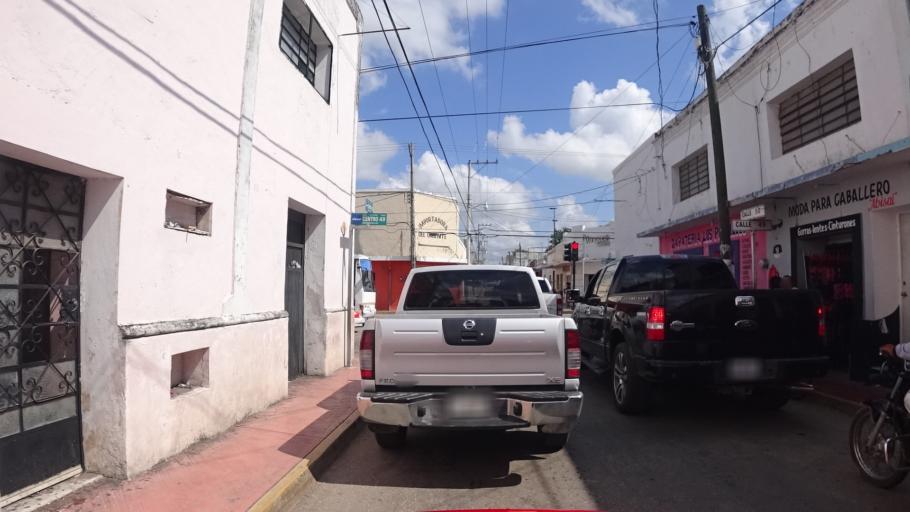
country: MX
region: Yucatan
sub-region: Tizimin
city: Tizimin
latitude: 21.1444
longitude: -88.1515
